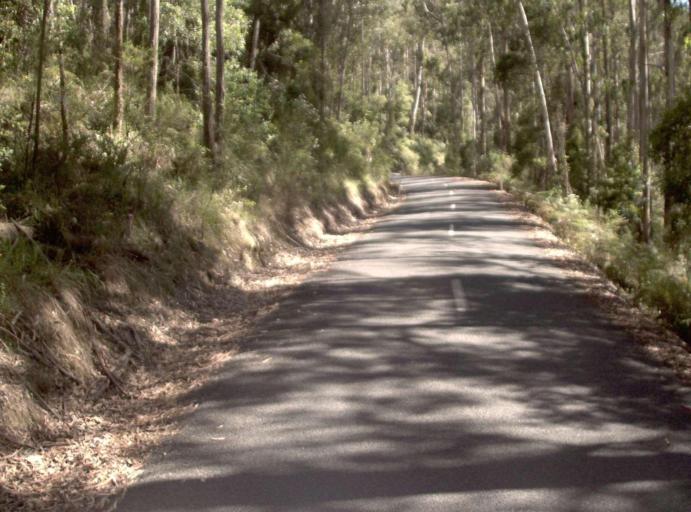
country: AU
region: New South Wales
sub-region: Bombala
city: Bombala
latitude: -37.3814
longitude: 148.6255
